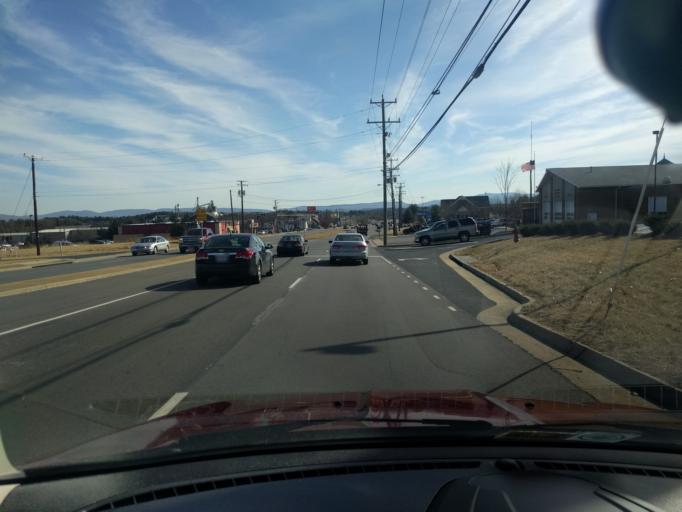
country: US
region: Virginia
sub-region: City of Staunton
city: Staunton
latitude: 38.1374
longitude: -79.0466
